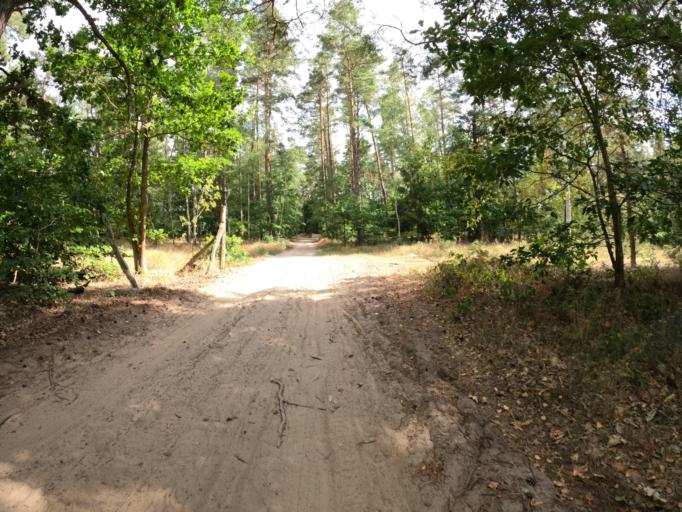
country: DE
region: Brandenburg
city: Lychen
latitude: 53.2764
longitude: 13.4350
